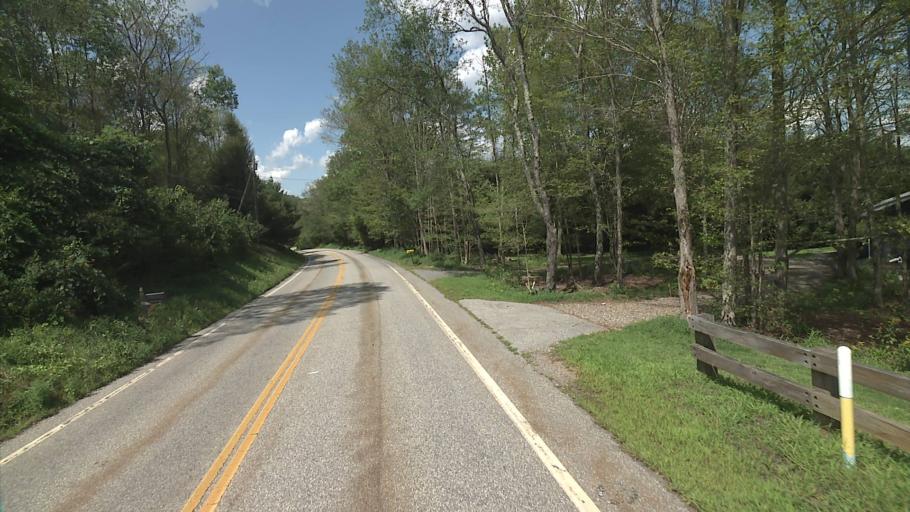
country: US
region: Connecticut
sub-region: Tolland County
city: Storrs
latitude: 41.8166
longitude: -72.1702
